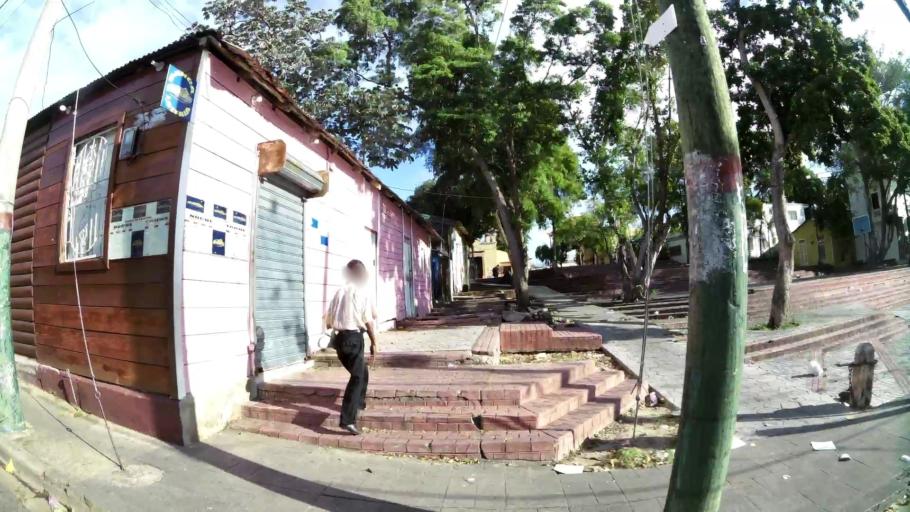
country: DO
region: Nacional
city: San Carlos
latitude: 18.4774
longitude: -69.8861
